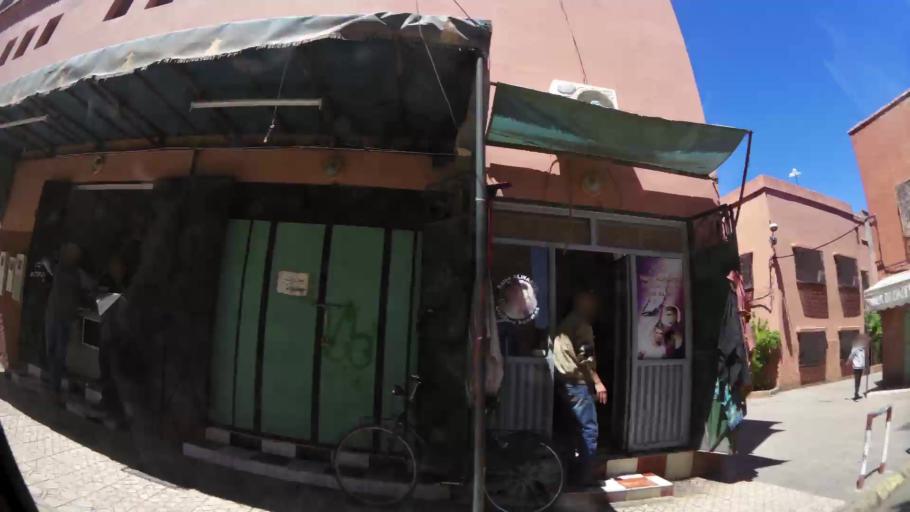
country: MA
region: Marrakech-Tensift-Al Haouz
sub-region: Marrakech
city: Marrakesh
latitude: 31.6529
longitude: -7.9909
